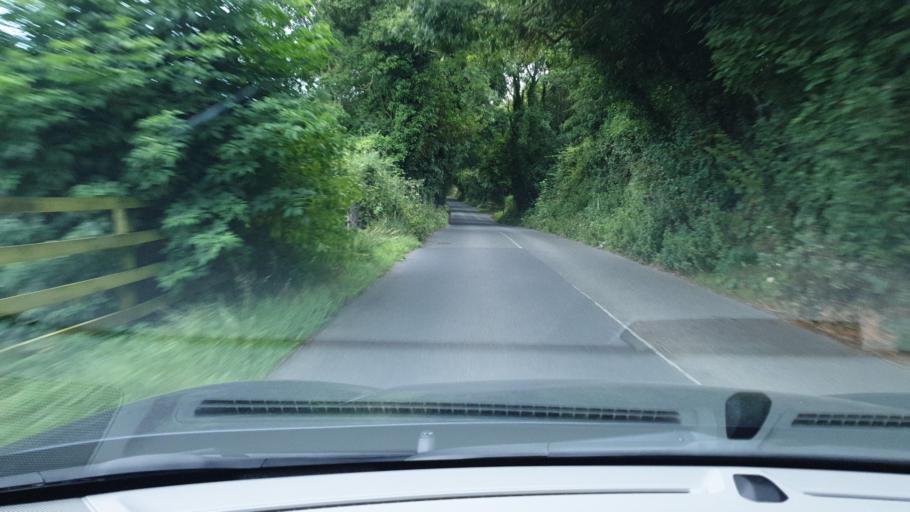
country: IE
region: Leinster
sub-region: South Dublin
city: Saggart
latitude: 53.2659
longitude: -6.4473
